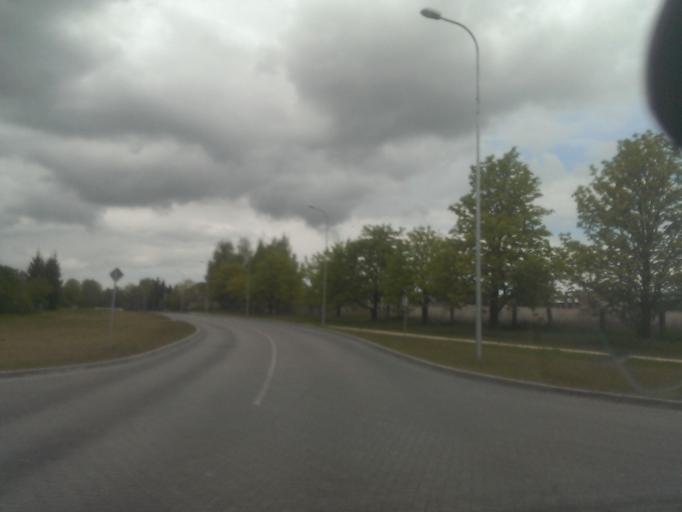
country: LV
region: Kuldigas Rajons
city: Kuldiga
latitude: 56.9798
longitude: 21.9490
